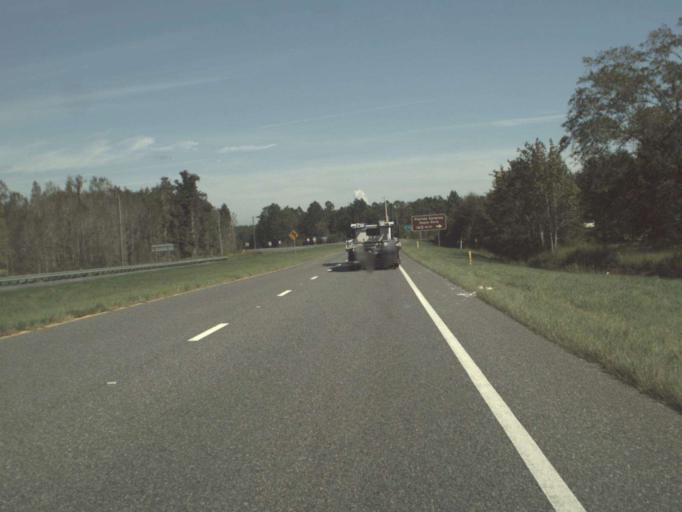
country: US
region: Florida
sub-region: Washington County
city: Chipley
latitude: 30.7216
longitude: -85.3892
